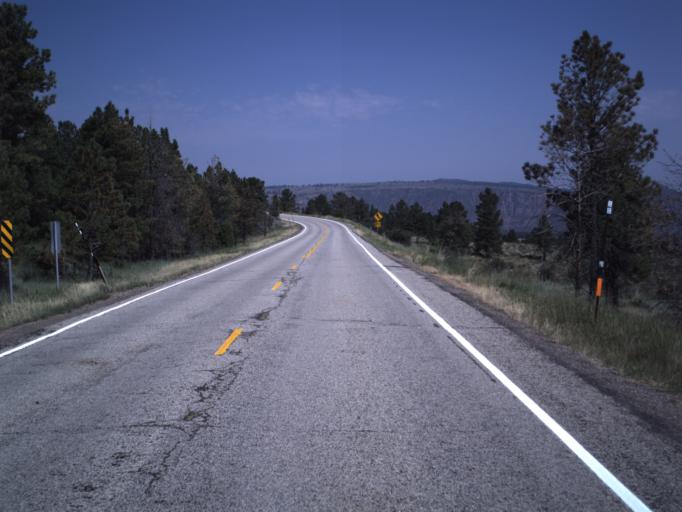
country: US
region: Utah
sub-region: Daggett County
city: Manila
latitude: 40.8698
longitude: -109.4915
